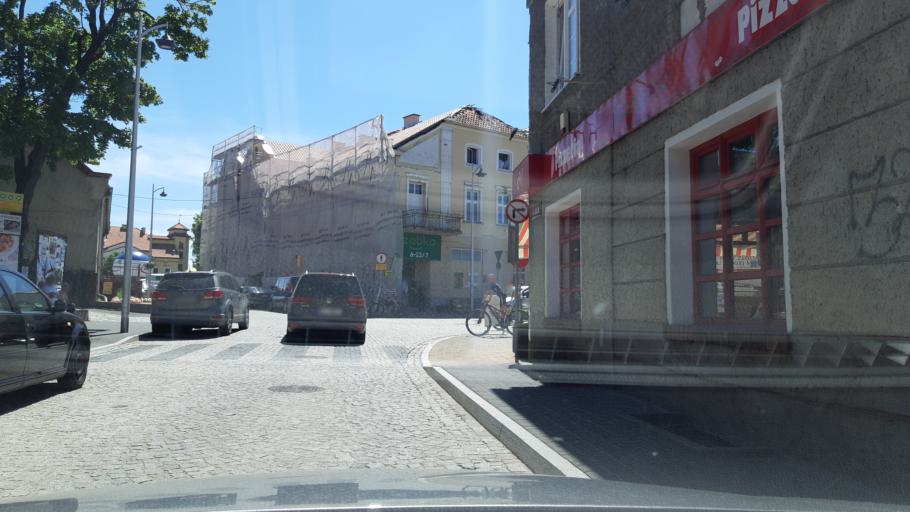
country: PL
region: Warmian-Masurian Voivodeship
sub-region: Powiat mragowski
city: Mikolajki
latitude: 53.8014
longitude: 21.5720
